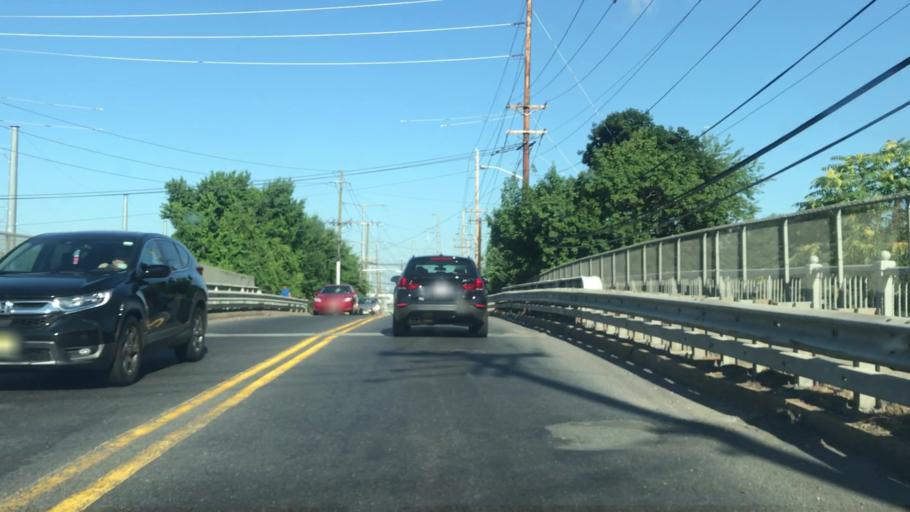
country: US
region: New Jersey
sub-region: Bergen County
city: Ridgefield
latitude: 40.8334
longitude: -74.0112
